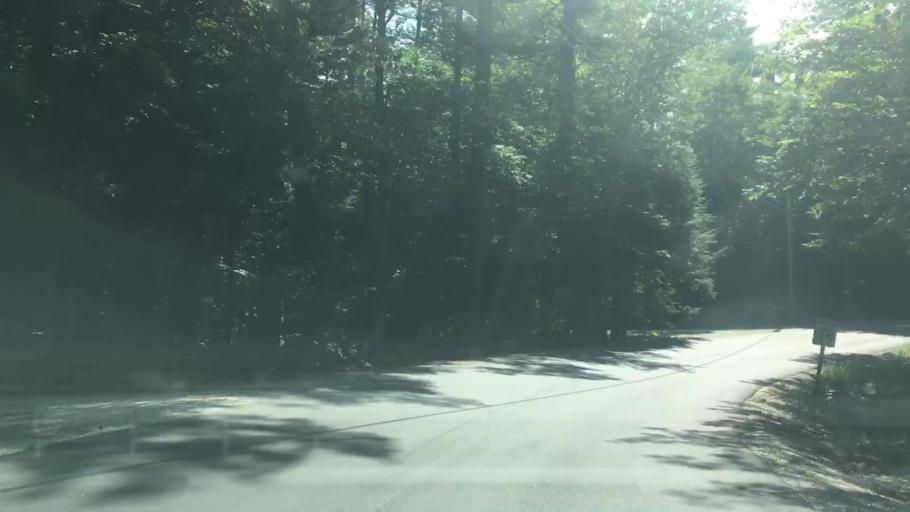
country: US
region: Maine
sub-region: Androscoggin County
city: Poland
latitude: 44.0142
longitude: -70.3924
